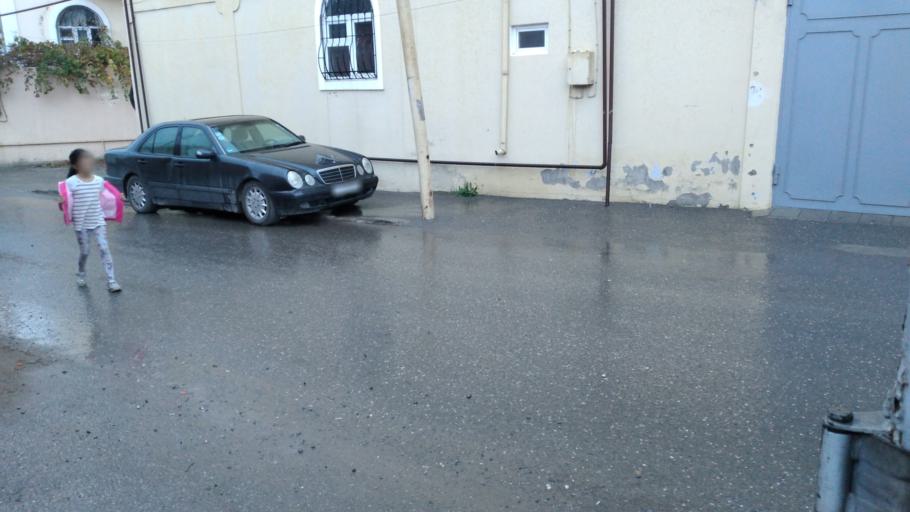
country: AZ
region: Baki
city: Bilajari
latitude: 40.4301
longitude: 49.8034
